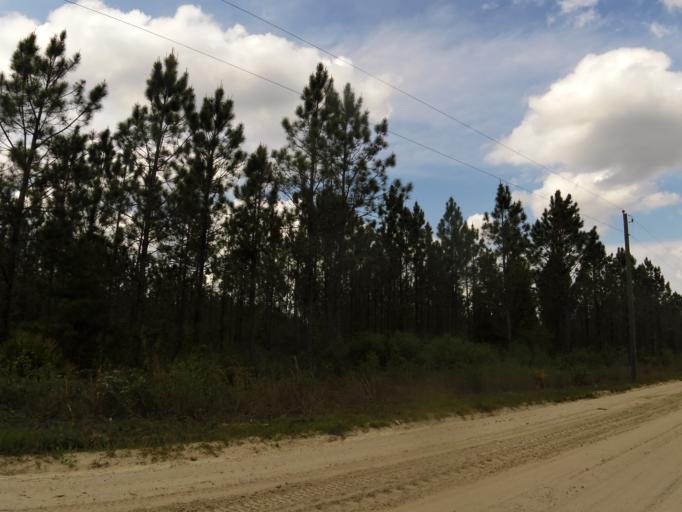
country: US
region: Georgia
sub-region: Charlton County
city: Folkston
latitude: 30.9450
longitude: -82.0004
